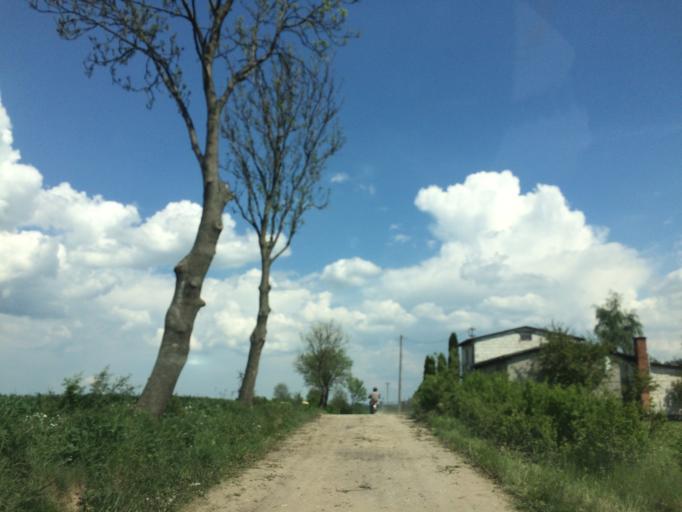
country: PL
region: Warmian-Masurian Voivodeship
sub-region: Powiat nowomiejski
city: Nowe Miasto Lubawskie
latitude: 53.4489
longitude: 19.5758
